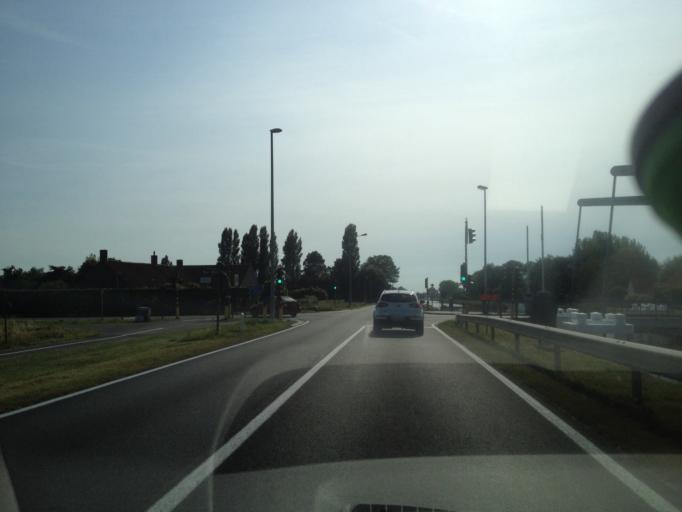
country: BE
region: Flanders
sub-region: Provincie West-Vlaanderen
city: Gistel
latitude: 51.1815
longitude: 2.9627
